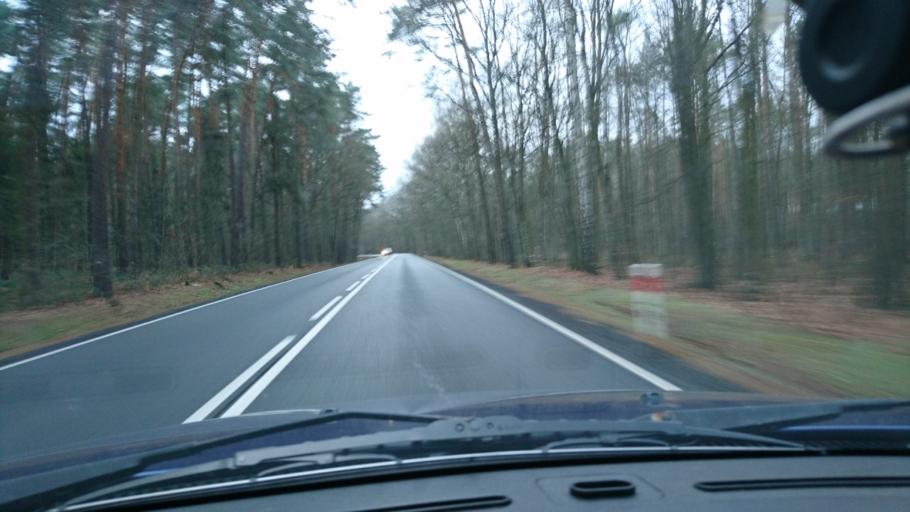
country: PL
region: Opole Voivodeship
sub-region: Powiat kluczborski
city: Kluczbork
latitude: 50.9435
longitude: 18.3226
